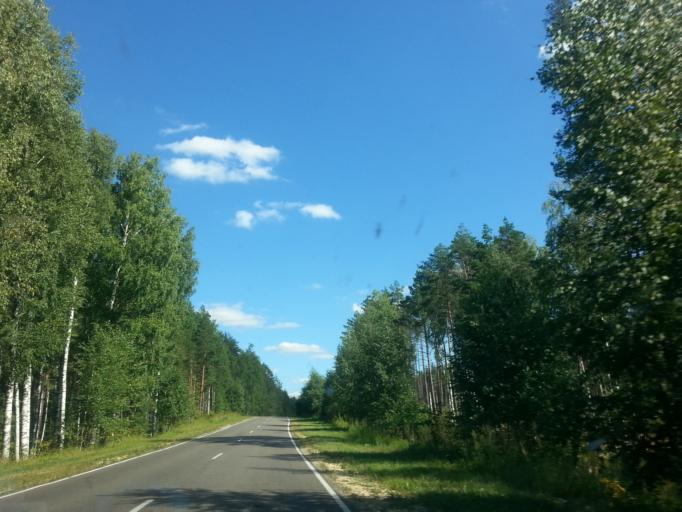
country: RU
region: Nizjnij Novgorod
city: Taremskoye
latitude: 56.0130
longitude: 42.9678
